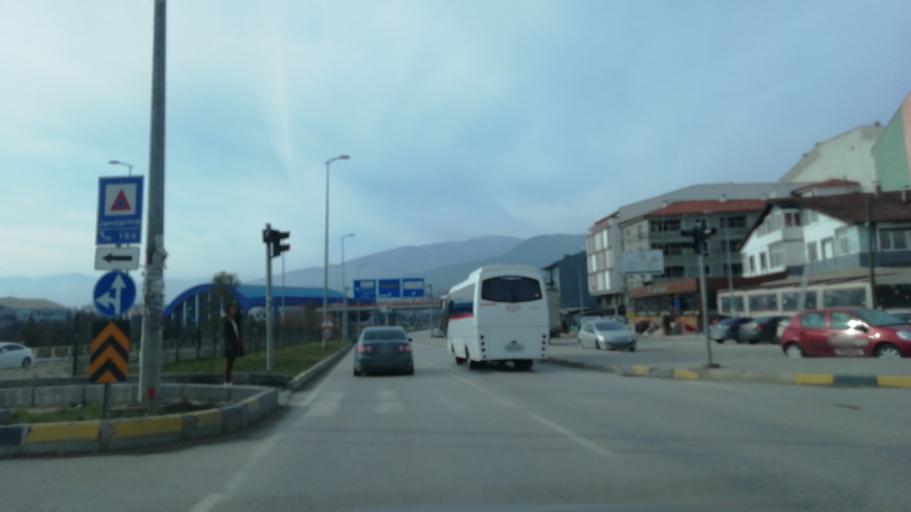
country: TR
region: Karabuk
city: Karabuk
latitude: 41.2166
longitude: 32.6605
